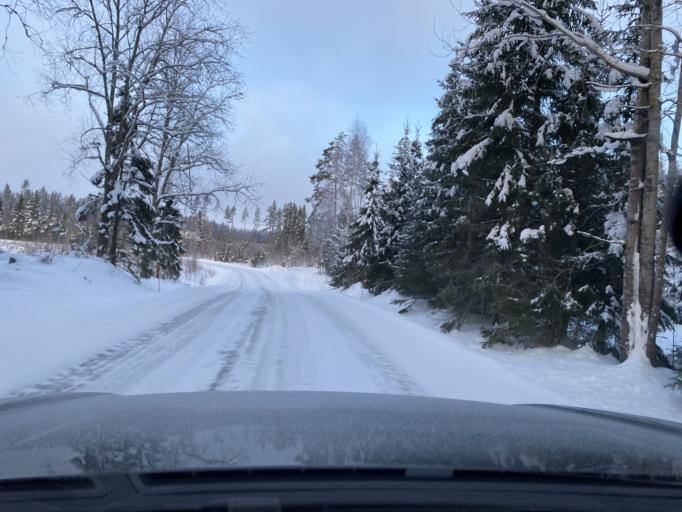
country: FI
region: Haeme
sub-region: Forssa
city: Tammela
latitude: 60.8643
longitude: 23.8779
